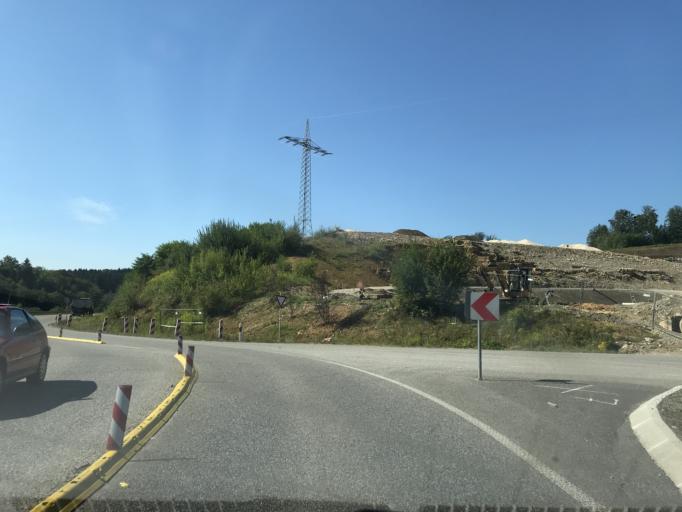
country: DE
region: Baden-Wuerttemberg
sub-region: Freiburg Region
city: Rheinfelden (Baden)
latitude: 47.5902
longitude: 7.7890
